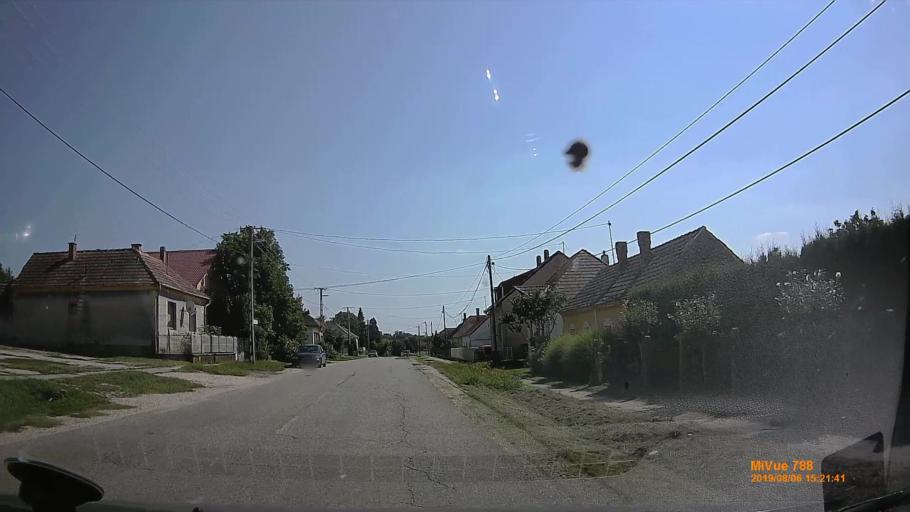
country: HR
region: Koprivnicko-Krizevacka
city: Drnje
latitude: 46.2743
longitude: 16.9488
